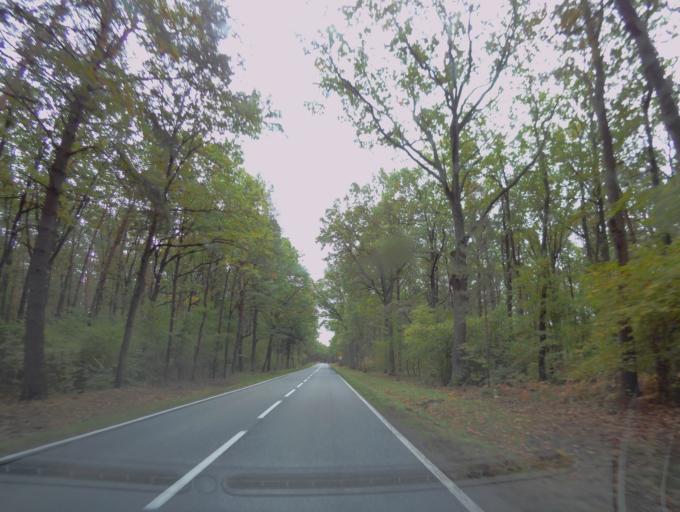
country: PL
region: Subcarpathian Voivodeship
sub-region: Powiat nizanski
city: Krzeszow
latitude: 50.3880
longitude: 22.3057
